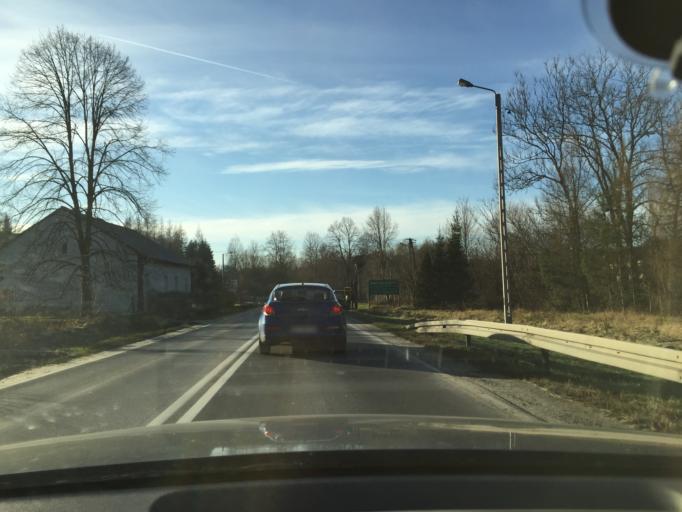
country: PL
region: Lesser Poland Voivodeship
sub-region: Powiat wadowicki
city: Izdebnik
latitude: 49.8751
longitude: 19.7762
